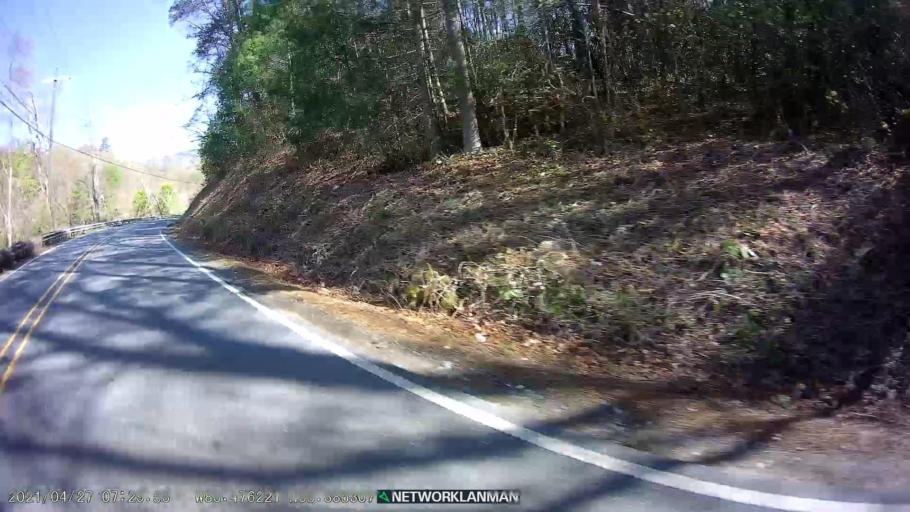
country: US
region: North Carolina
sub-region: Swain County
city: Bryson City
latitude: 35.3854
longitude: -83.4764
